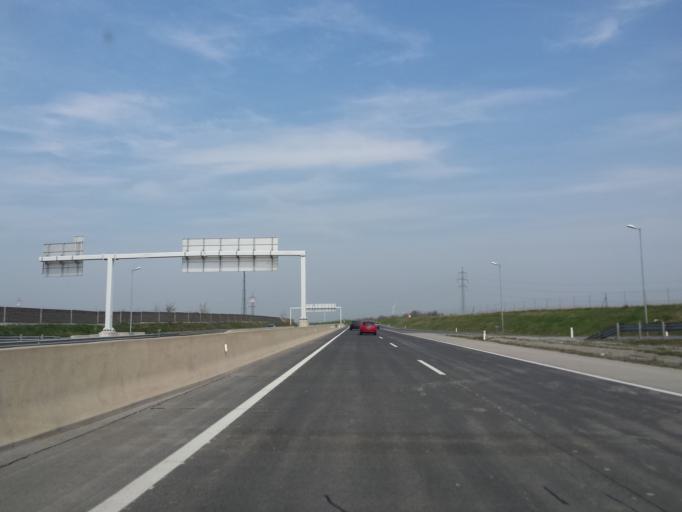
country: AT
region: Lower Austria
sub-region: Politischer Bezirk Ganserndorf
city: Aderklaa
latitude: 48.2822
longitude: 16.5124
